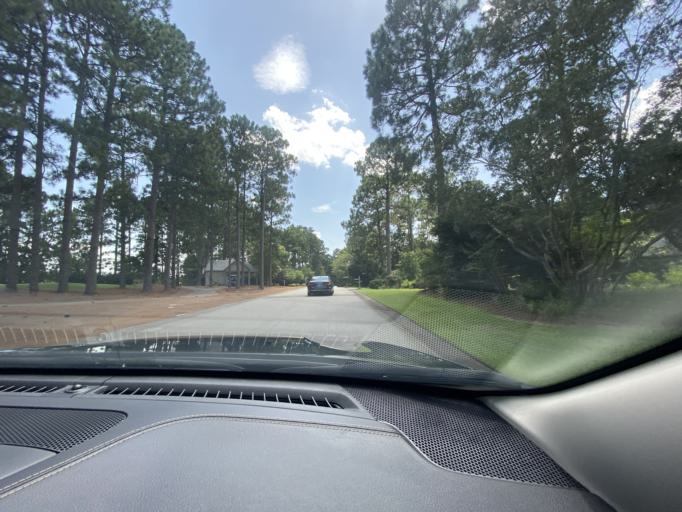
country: US
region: North Carolina
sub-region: Moore County
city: Pinehurst
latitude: 35.1881
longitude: -79.4343
